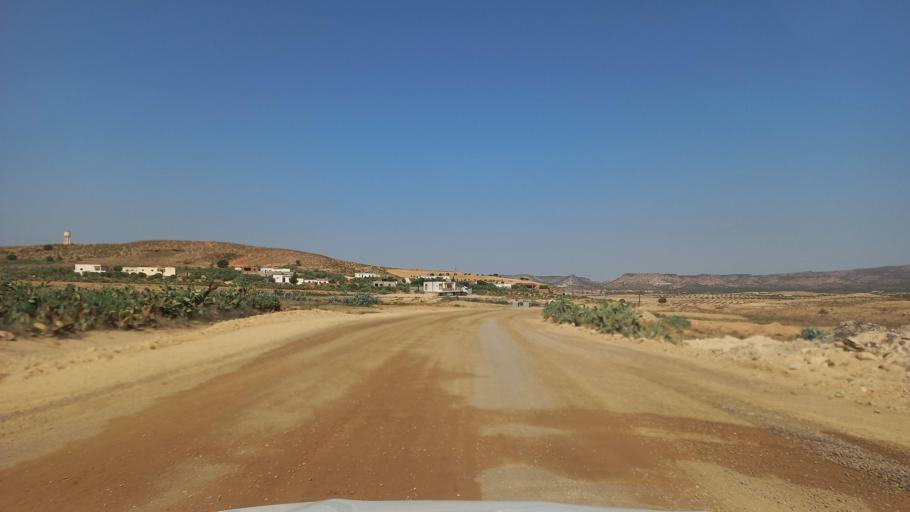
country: TN
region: Al Qasrayn
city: Sbiba
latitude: 35.3834
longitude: 9.0276
